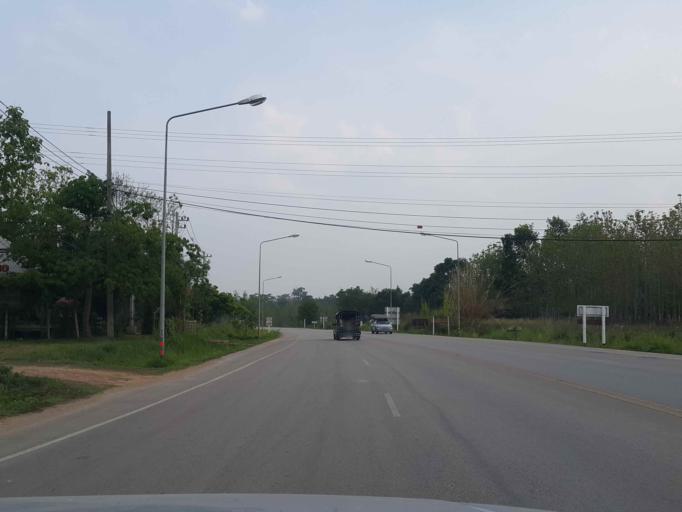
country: TH
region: Chiang Mai
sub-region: Amphoe Chiang Dao
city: Chiang Dao
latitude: 19.3770
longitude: 98.9462
